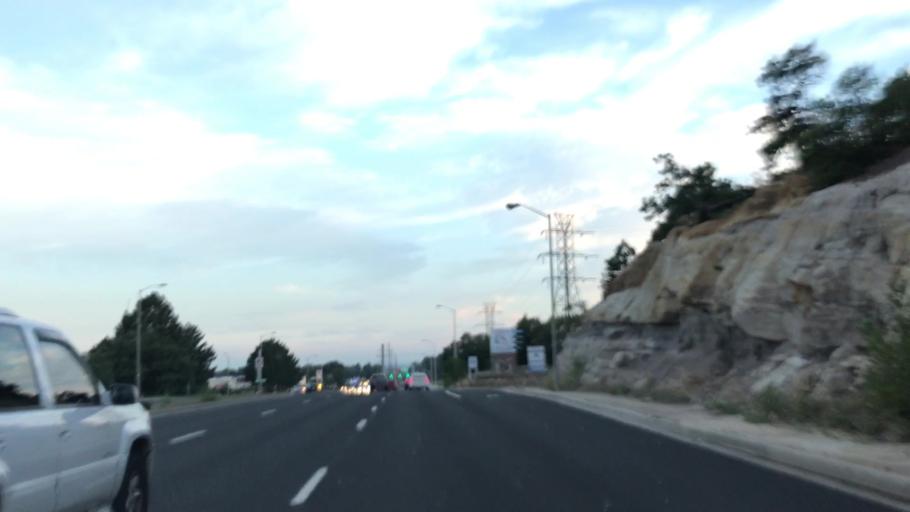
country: US
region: Colorado
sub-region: El Paso County
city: Cimarron Hills
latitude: 38.8711
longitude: -104.7572
